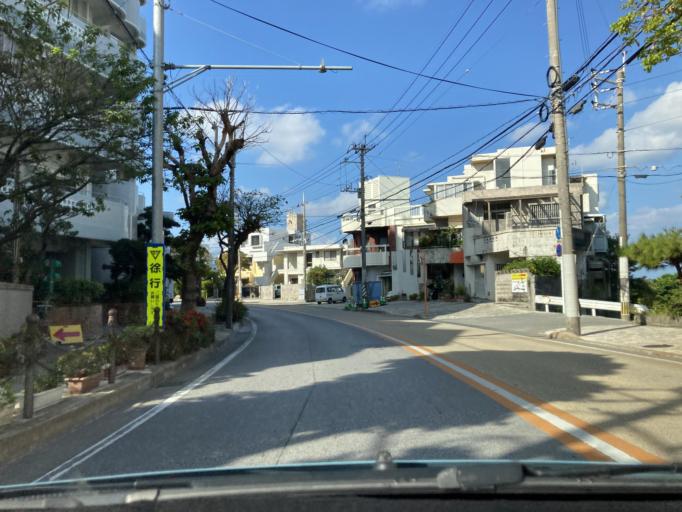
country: JP
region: Okinawa
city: Naha-shi
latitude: 26.2235
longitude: 127.7147
